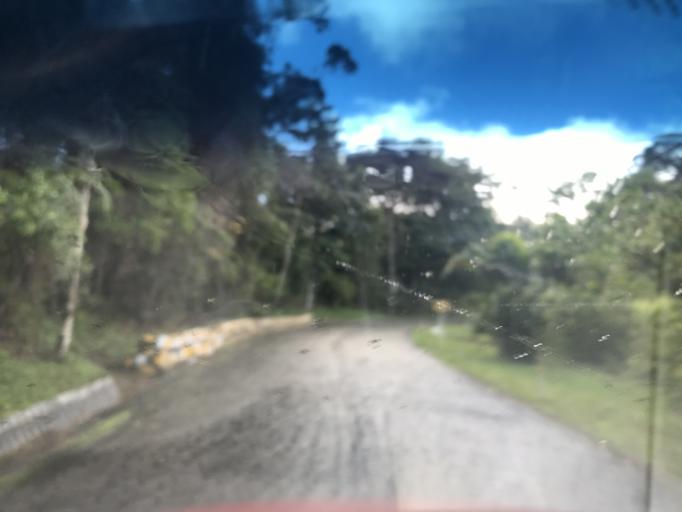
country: BR
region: Bahia
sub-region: Gandu
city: Gandu
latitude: -13.9025
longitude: -39.4616
